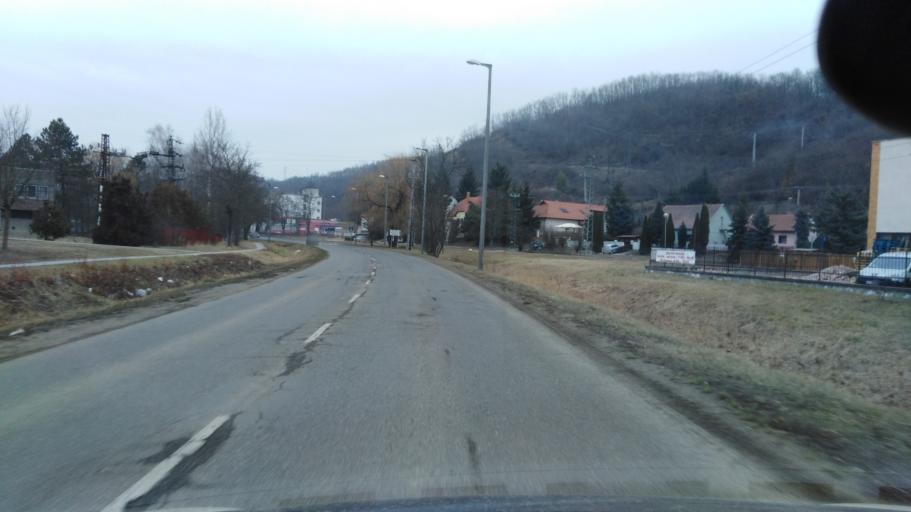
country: HU
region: Nograd
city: Salgotarjan
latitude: 48.0783
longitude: 19.7921
